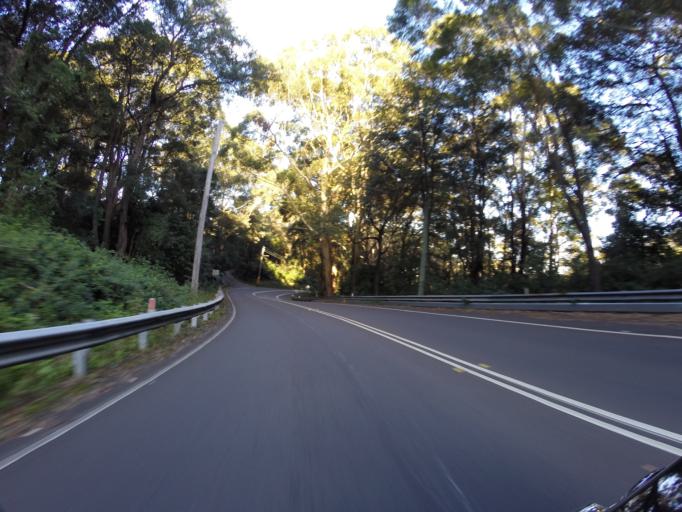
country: AU
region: New South Wales
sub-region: Wollongong
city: Helensburgh
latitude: -34.2244
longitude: 150.9853
